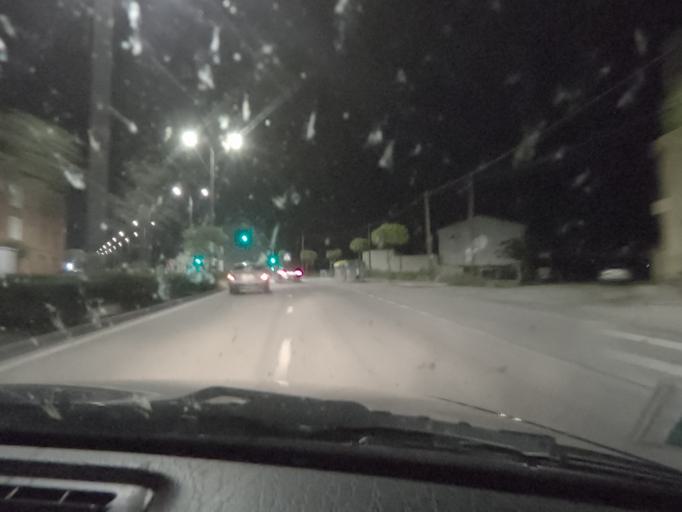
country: ES
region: Extremadura
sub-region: Provincia de Caceres
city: Moraleja
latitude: 40.0724
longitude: -6.6593
